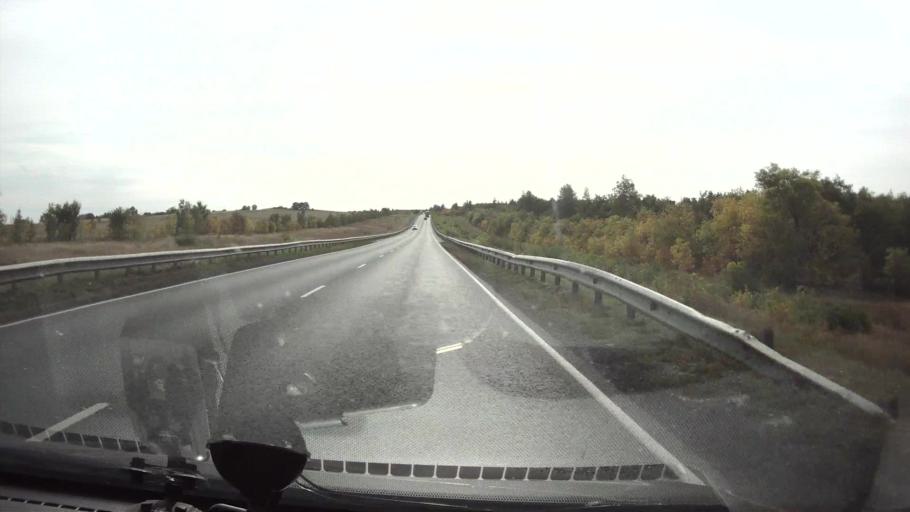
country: RU
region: Saratov
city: Balakovo
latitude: 52.1753
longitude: 47.8354
